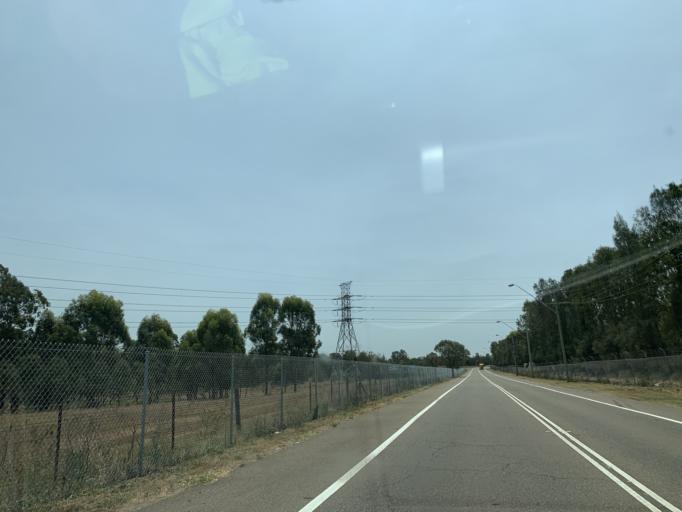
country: AU
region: New South Wales
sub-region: Fairfield
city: Horsley Park
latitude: -33.8068
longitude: 150.8641
